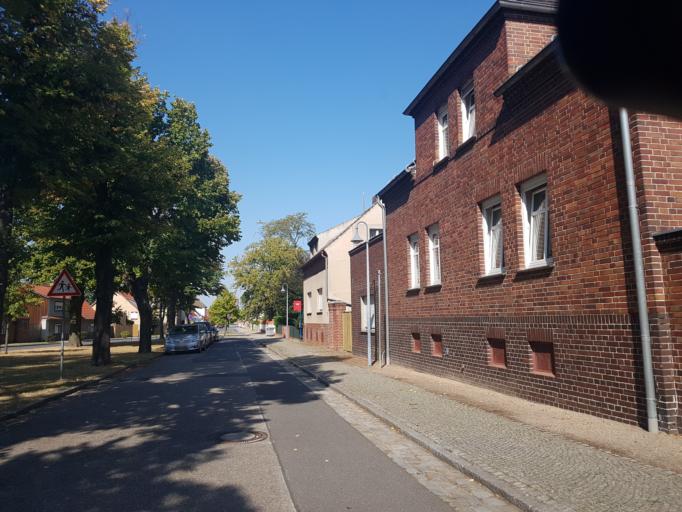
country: DE
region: Brandenburg
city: Finsterwalde
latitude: 51.6430
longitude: 13.7318
